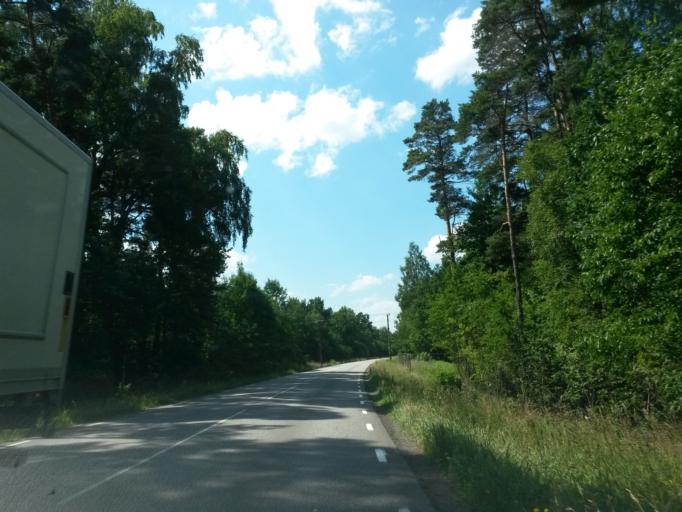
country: SE
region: Vaestra Goetaland
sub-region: Essunga Kommun
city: Nossebro
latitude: 58.1860
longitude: 12.7523
